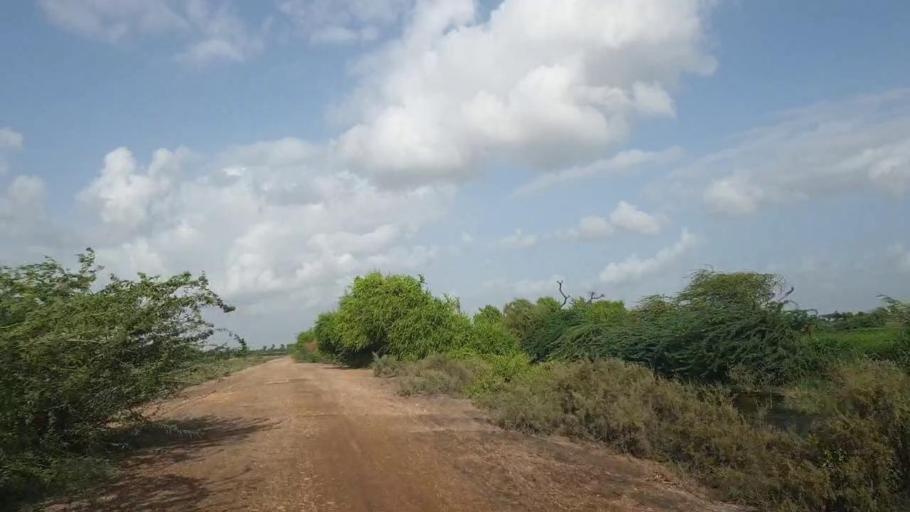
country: PK
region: Sindh
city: Kadhan
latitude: 24.6337
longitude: 69.0938
